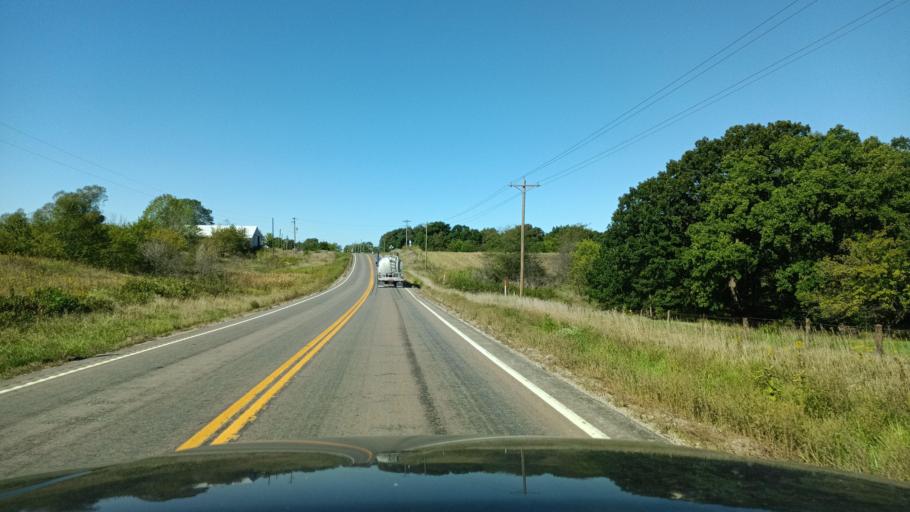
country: US
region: Missouri
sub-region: Scotland County
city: Memphis
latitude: 40.4544
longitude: -92.0155
